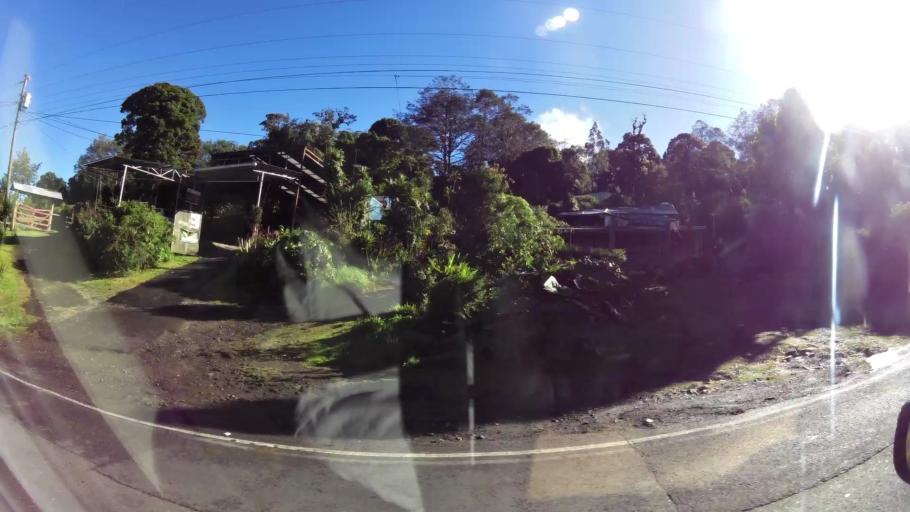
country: CR
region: San Jose
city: San Marcos
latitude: 9.7167
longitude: -83.9492
